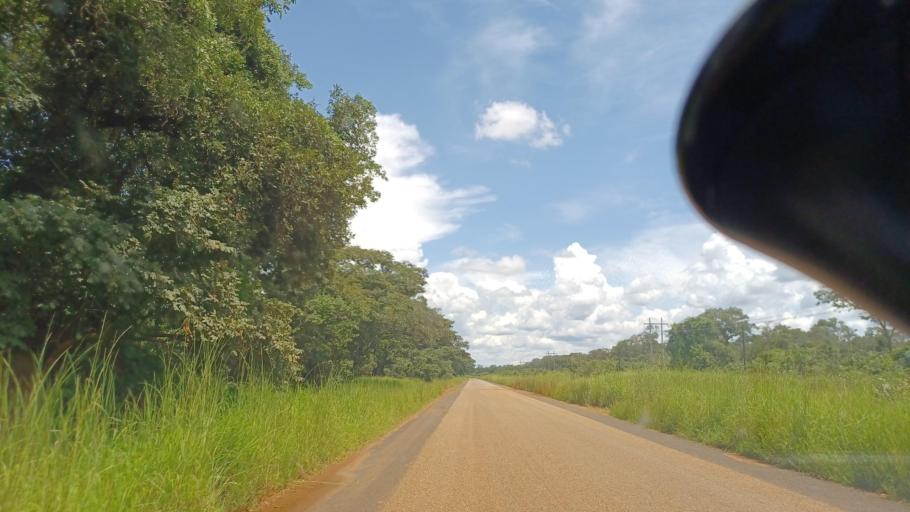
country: ZM
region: North-Western
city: Solwezi
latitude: -12.5743
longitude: 26.1338
